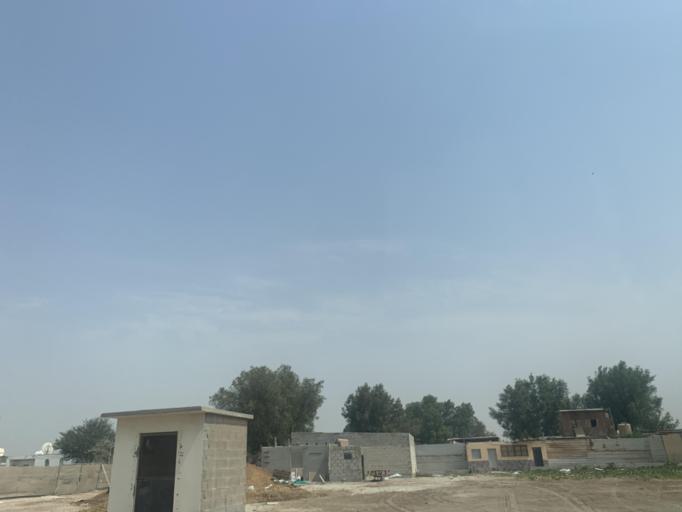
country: BH
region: Manama
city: Jidd Hafs
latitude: 26.2048
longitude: 50.5040
